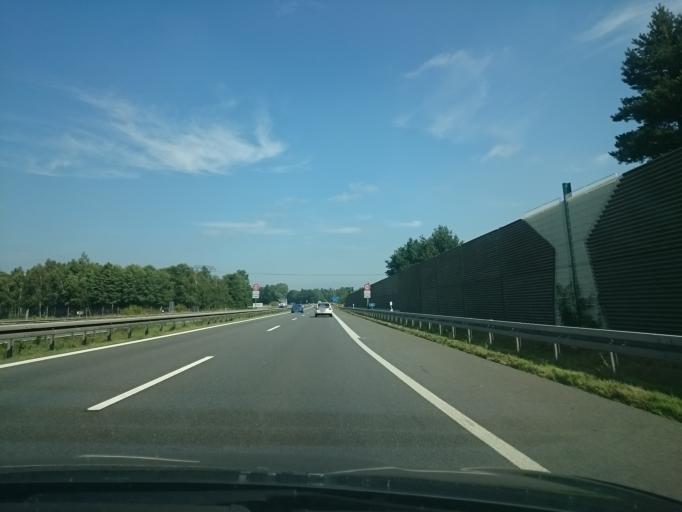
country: DE
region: Brandenburg
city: Calau
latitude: 51.7887
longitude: 13.8792
